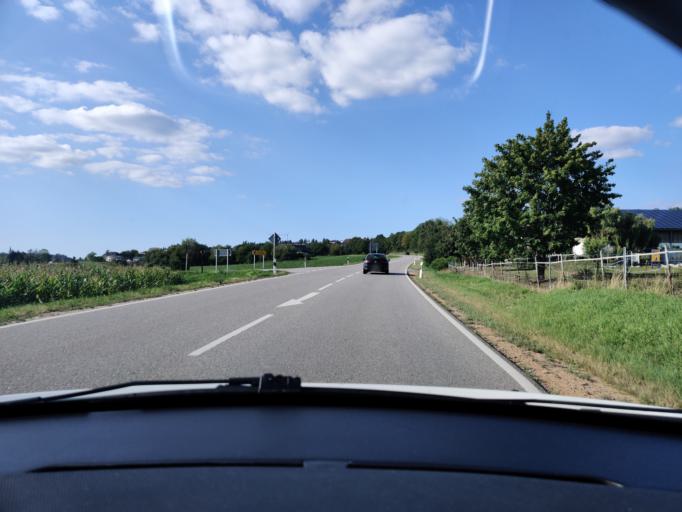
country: DE
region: Bavaria
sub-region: Upper Palatinate
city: Schwarzenfeld
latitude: 49.3818
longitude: 12.1561
